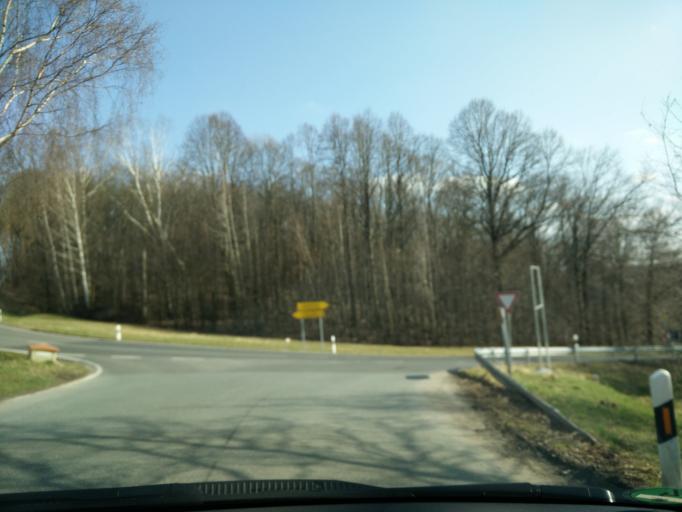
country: DE
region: Saxony
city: Rochlitz
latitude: 51.0544
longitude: 12.8122
